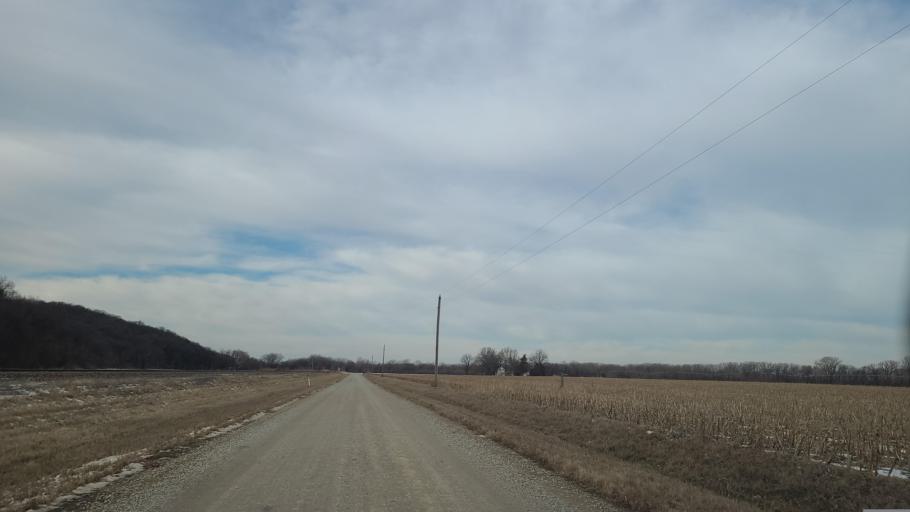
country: US
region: Kansas
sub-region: Jefferson County
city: Oskaloosa
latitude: 39.0601
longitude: -95.4549
